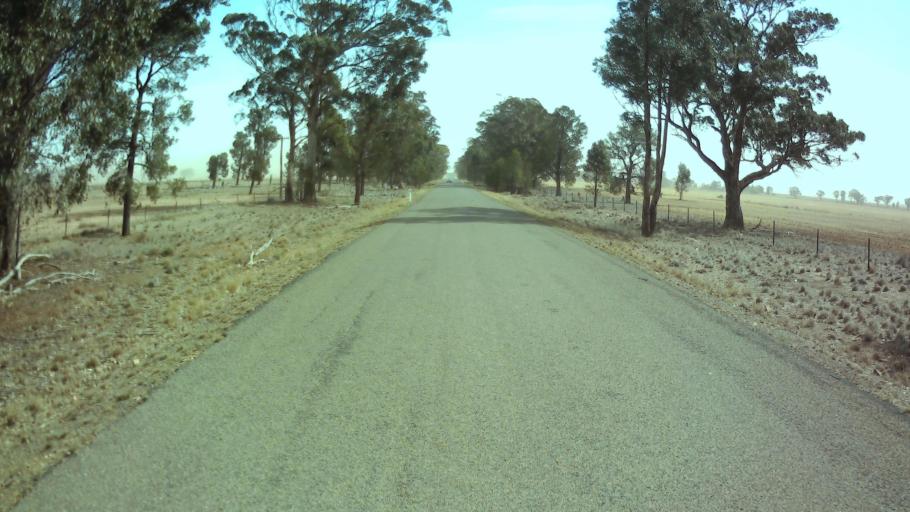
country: AU
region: New South Wales
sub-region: Weddin
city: Grenfell
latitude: -33.7583
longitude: 147.9893
